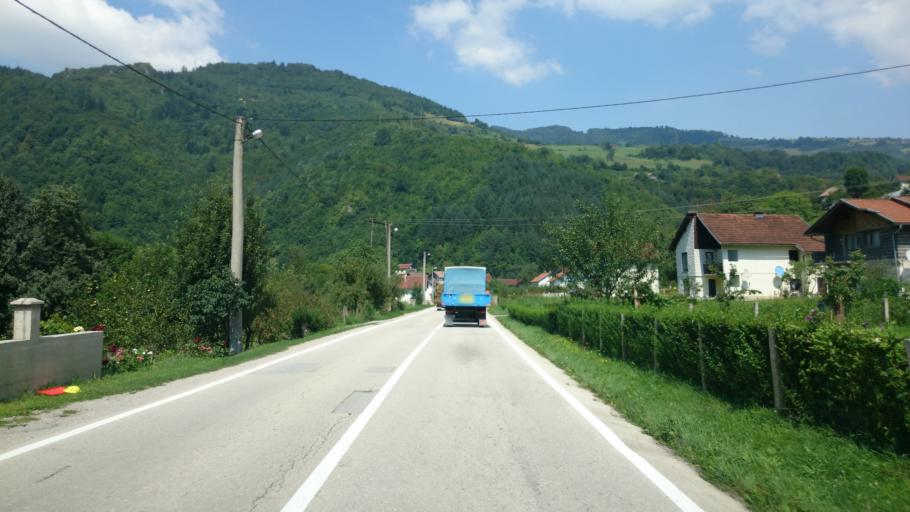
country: BA
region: Federation of Bosnia and Herzegovina
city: Donji Vakuf
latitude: 44.2278
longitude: 17.3136
